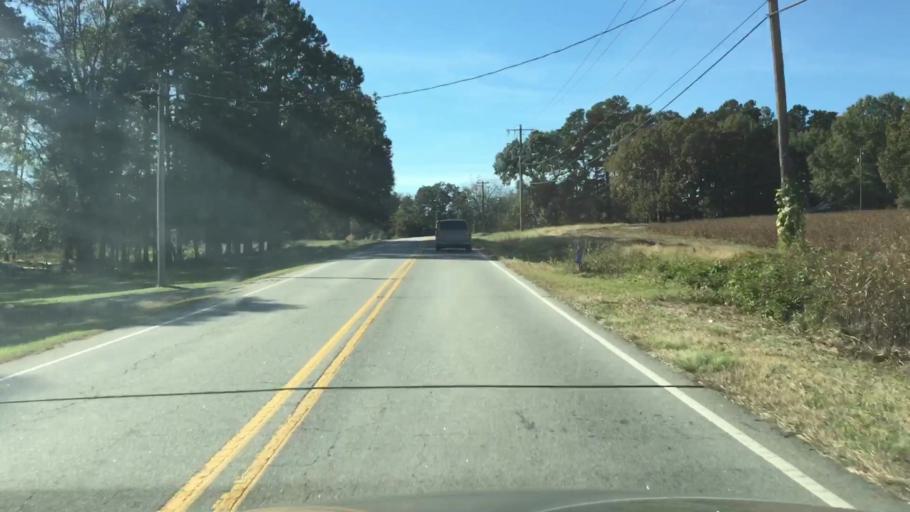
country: US
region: North Carolina
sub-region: Rowan County
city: China Grove
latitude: 35.6478
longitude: -80.6332
